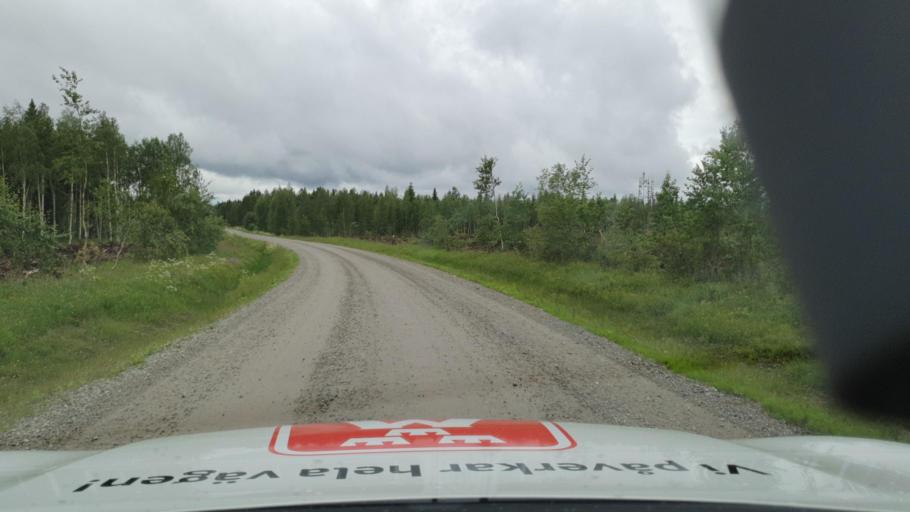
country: SE
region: Vaesterbotten
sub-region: Dorotea Kommun
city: Dorotea
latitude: 64.0881
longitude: 16.6760
